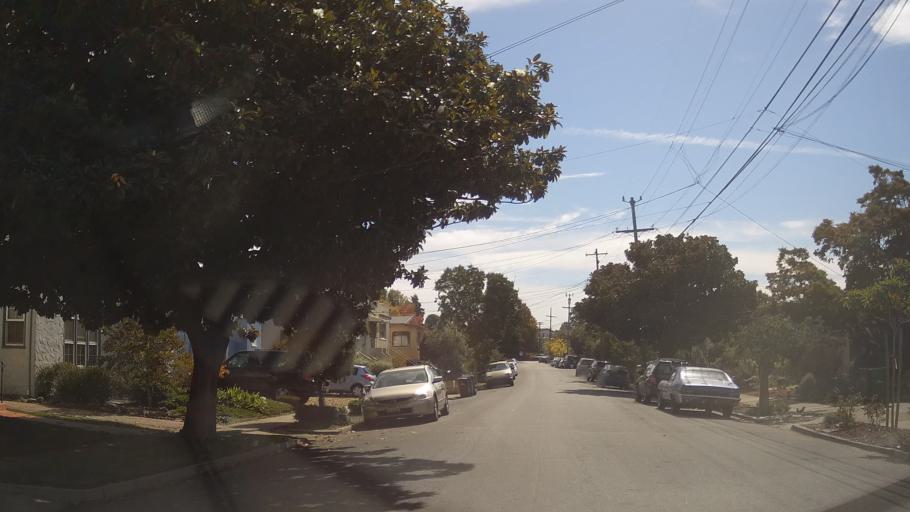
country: US
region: California
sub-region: Alameda County
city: Albany
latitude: 37.8862
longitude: -122.2904
